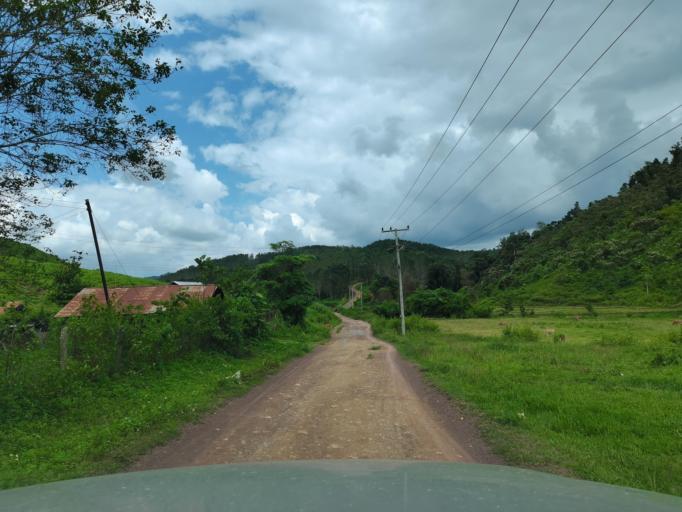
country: LA
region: Loungnamtha
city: Muang Long
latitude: 20.7007
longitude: 101.0187
